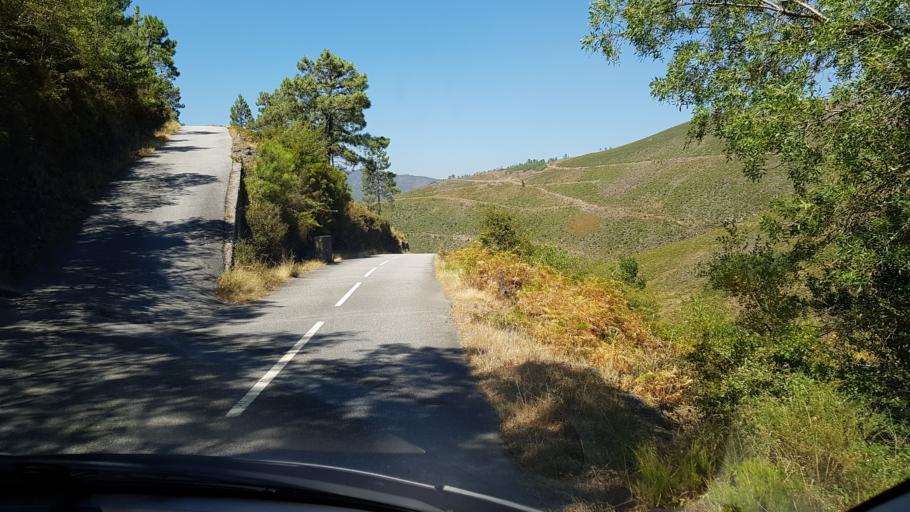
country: PT
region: Vila Real
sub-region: Mondim de Basto
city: Mondim de Basto
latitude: 41.3341
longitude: -7.8876
